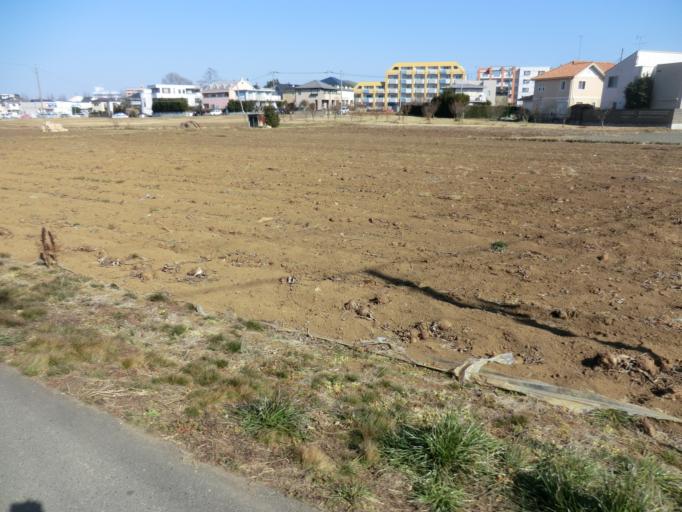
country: JP
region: Ibaraki
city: Naka
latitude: 36.0626
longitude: 140.1142
